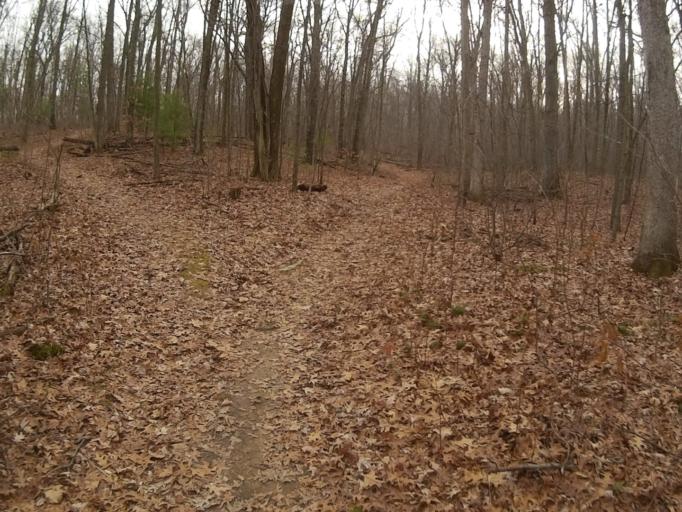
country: US
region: Pennsylvania
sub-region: Centre County
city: Park Forest Village
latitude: 40.7916
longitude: -77.9256
